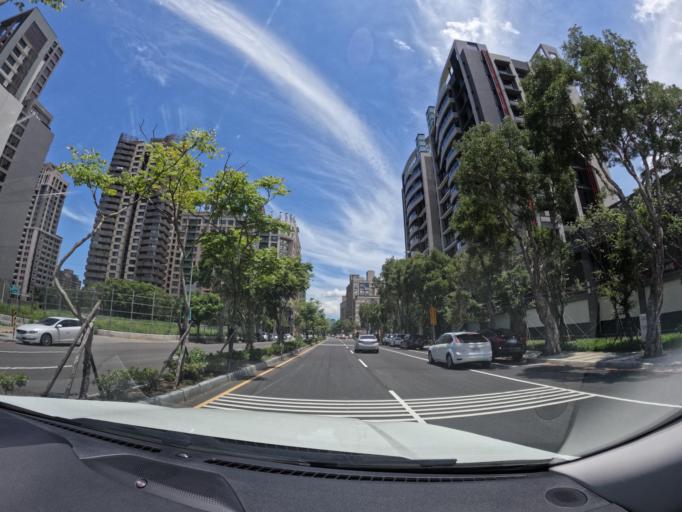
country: TW
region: Taiwan
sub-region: Taoyuan
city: Taoyuan
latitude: 25.0799
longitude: 121.3774
